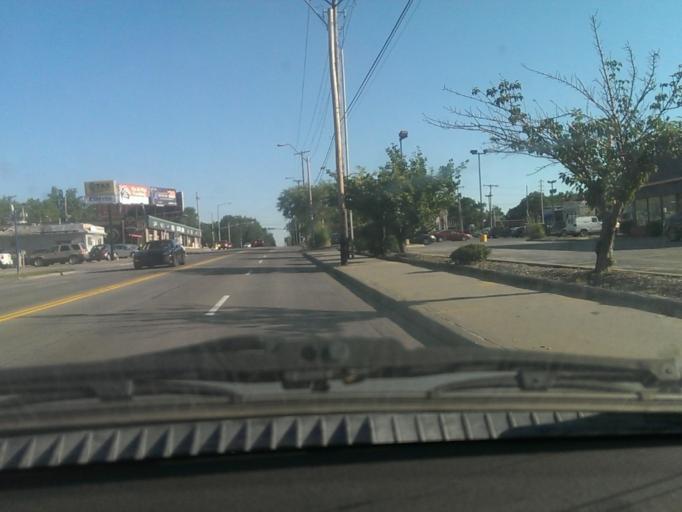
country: US
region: Kansas
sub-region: Johnson County
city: Leawood
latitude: 38.9758
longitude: -94.5950
